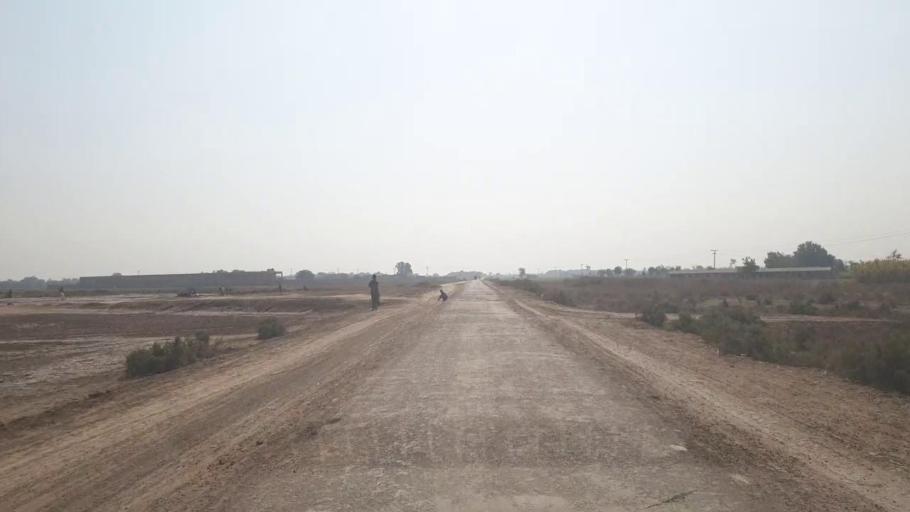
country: PK
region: Sindh
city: Tando Allahyar
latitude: 25.4747
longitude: 68.8068
